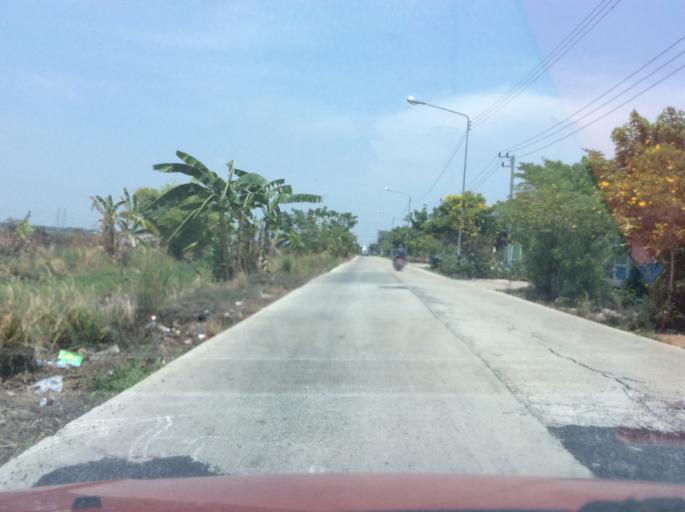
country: TH
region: Pathum Thani
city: Ban Lam Luk Ka
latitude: 13.9844
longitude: 100.7563
